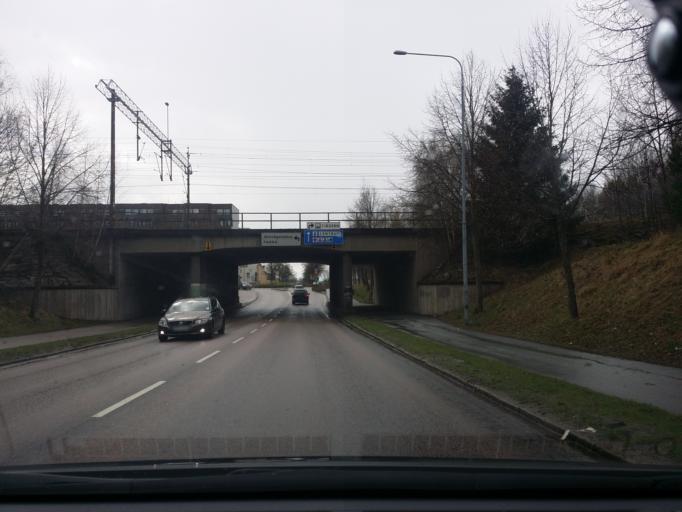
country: SE
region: Uppsala
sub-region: Enkopings Kommun
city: Enkoping
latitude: 59.6460
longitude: 17.0832
